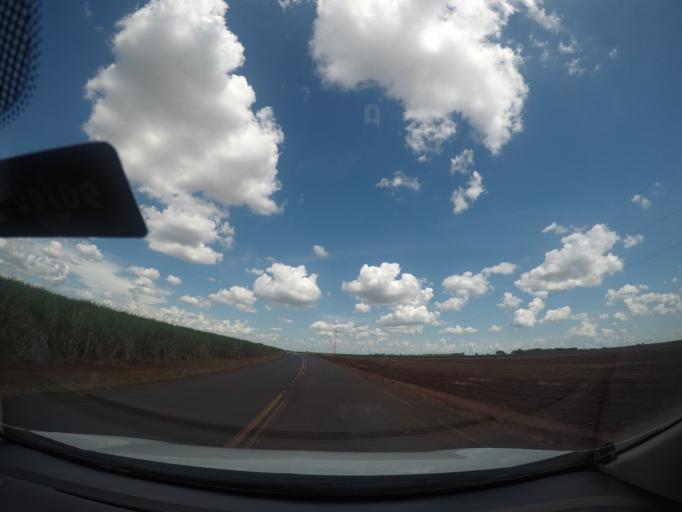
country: BR
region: Minas Gerais
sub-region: Frutal
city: Frutal
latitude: -19.8476
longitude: -48.7377
